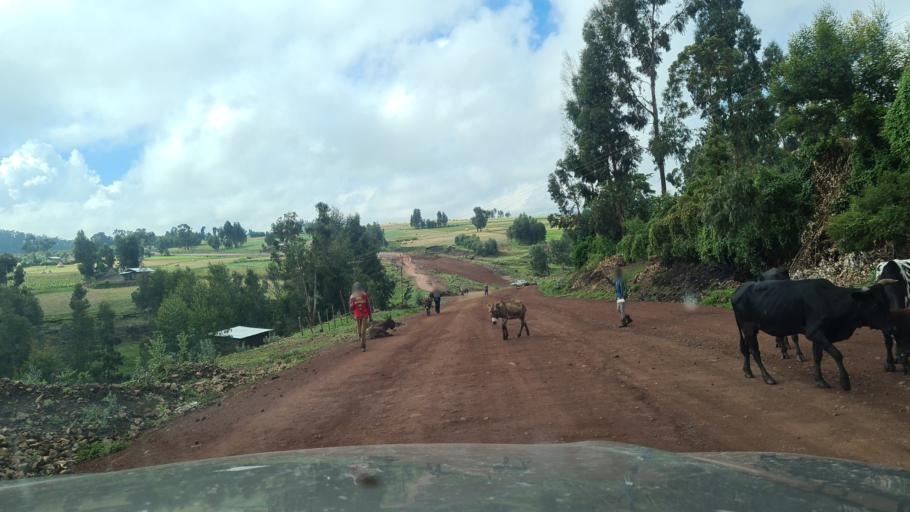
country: ET
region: Oromiya
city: Huruta
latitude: 8.1283
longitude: 39.4354
